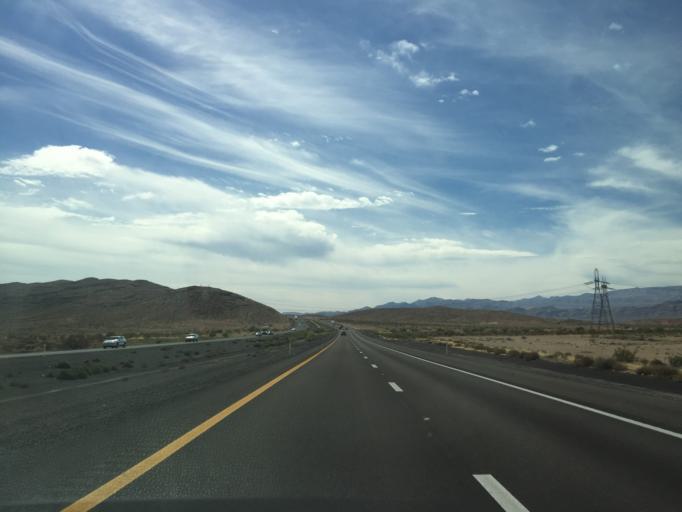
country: US
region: Nevada
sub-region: Clark County
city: Moapa Town
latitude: 36.4744
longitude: -114.8170
